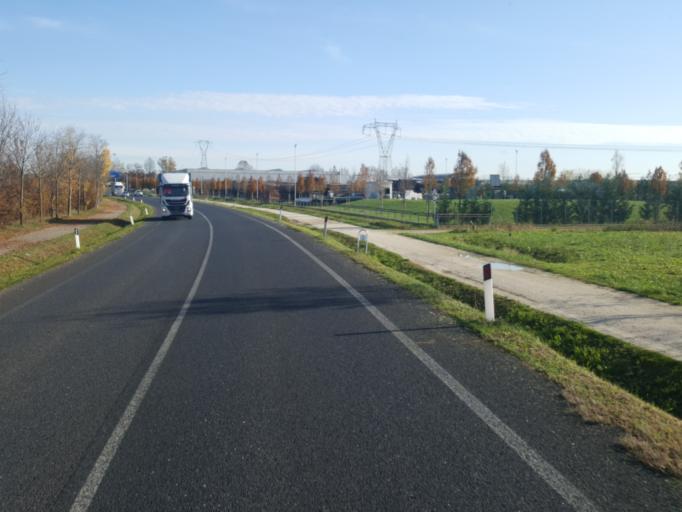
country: IT
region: Veneto
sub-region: Provincia di Treviso
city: Riese Pio X
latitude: 45.7179
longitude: 11.9158
